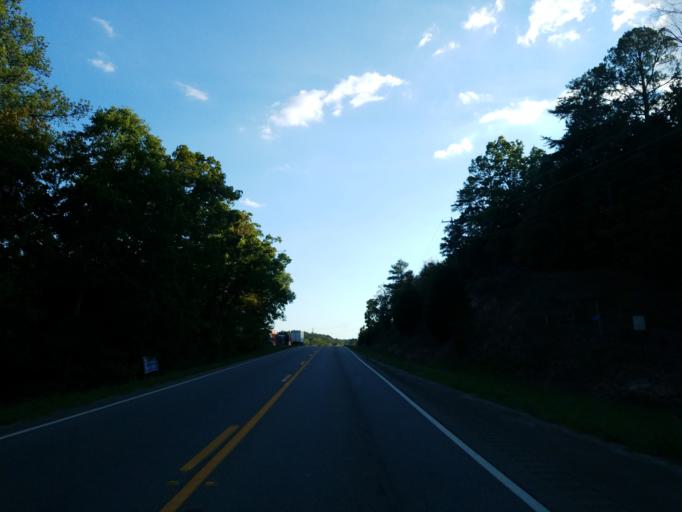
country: US
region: Georgia
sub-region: Murray County
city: Chatsworth
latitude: 34.5778
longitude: -84.7034
